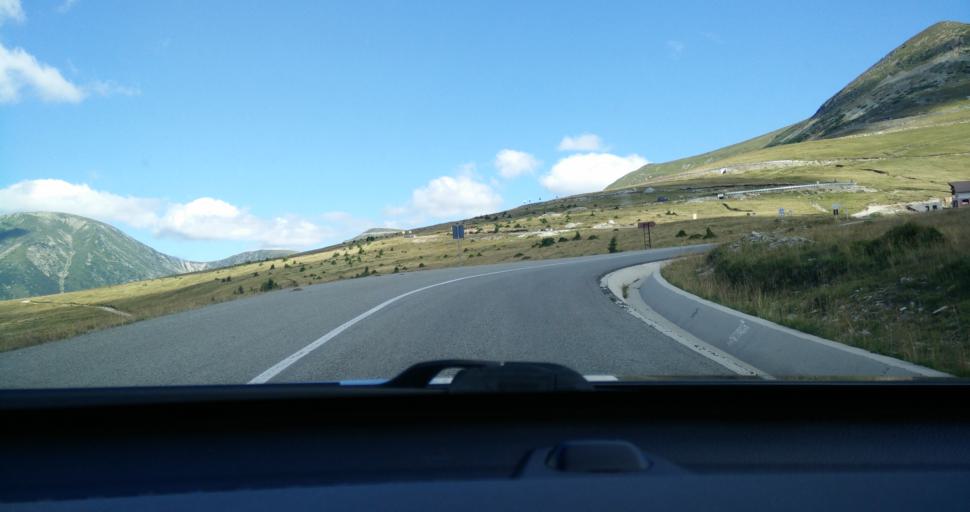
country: RO
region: Gorj
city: Novaci-Straini
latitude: 45.3122
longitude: 23.6826
